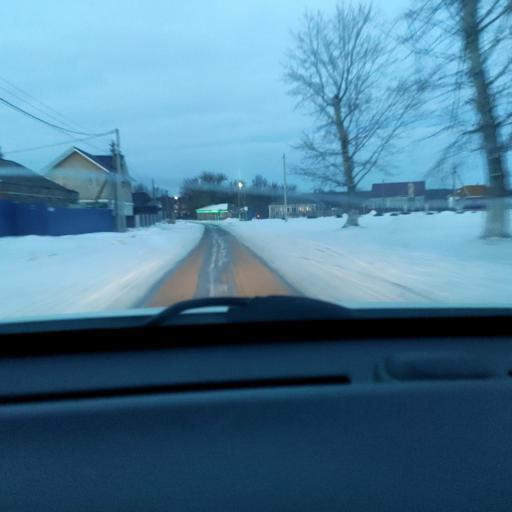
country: RU
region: Voronezj
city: Novaya Usman'
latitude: 51.6823
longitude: 39.3772
